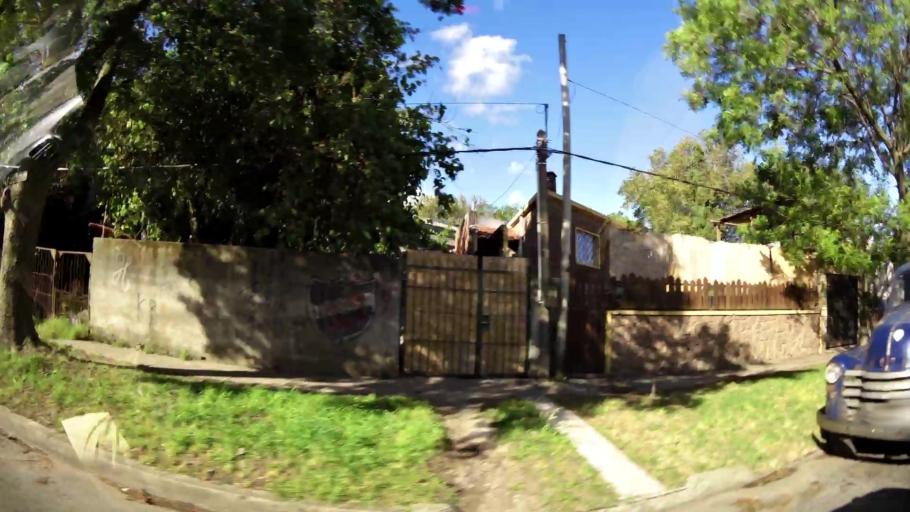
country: UY
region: Montevideo
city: Montevideo
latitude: -34.8505
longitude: -56.2134
